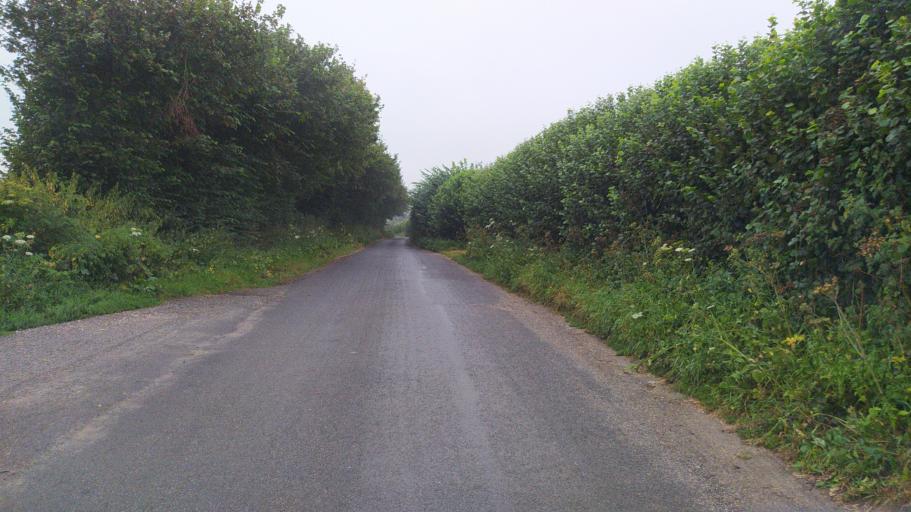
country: GB
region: England
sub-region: Wiltshire
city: Ansty
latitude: 51.0128
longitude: -2.1147
